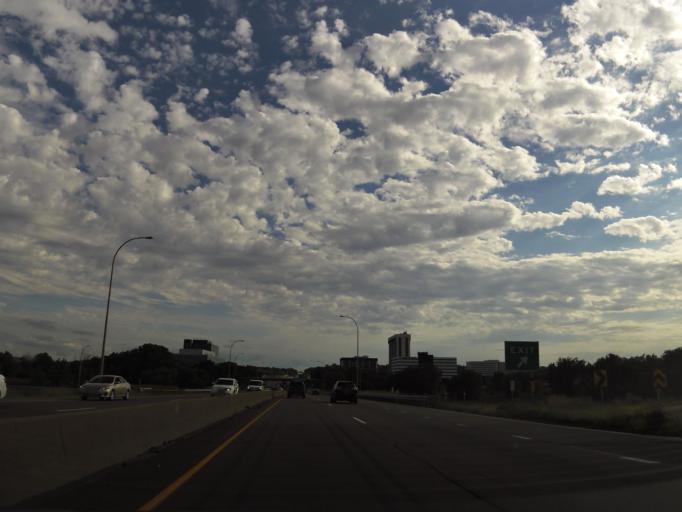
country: US
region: Minnesota
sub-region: Hennepin County
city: New Hope
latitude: 44.9826
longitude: -93.4008
